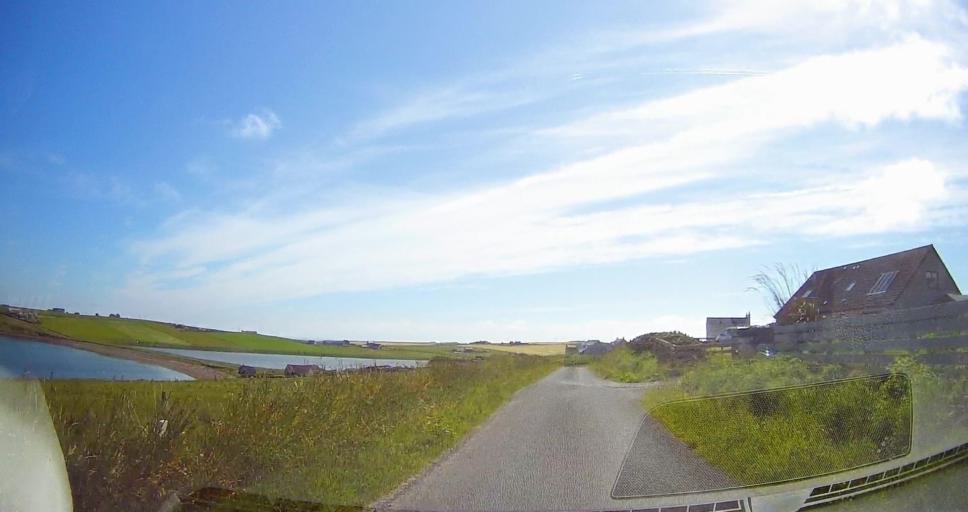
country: GB
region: Scotland
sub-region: Orkney Islands
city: Kirkwall
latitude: 58.8543
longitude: -2.9233
